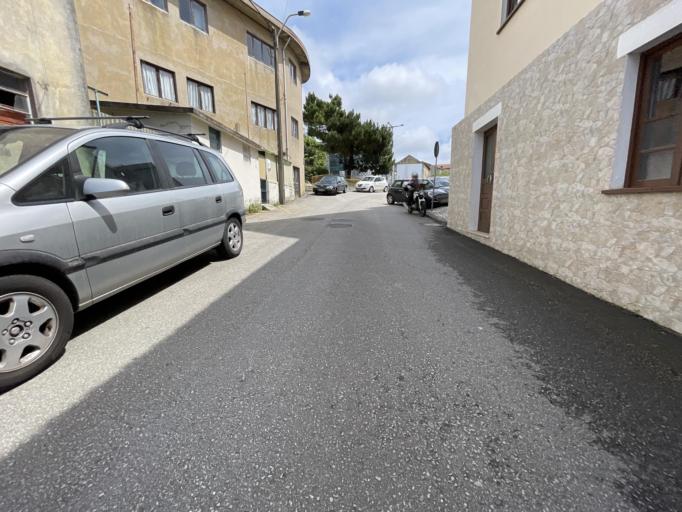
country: PT
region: Aveiro
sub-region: Ovar
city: Cortegaca
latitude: 40.9455
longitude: -8.6229
